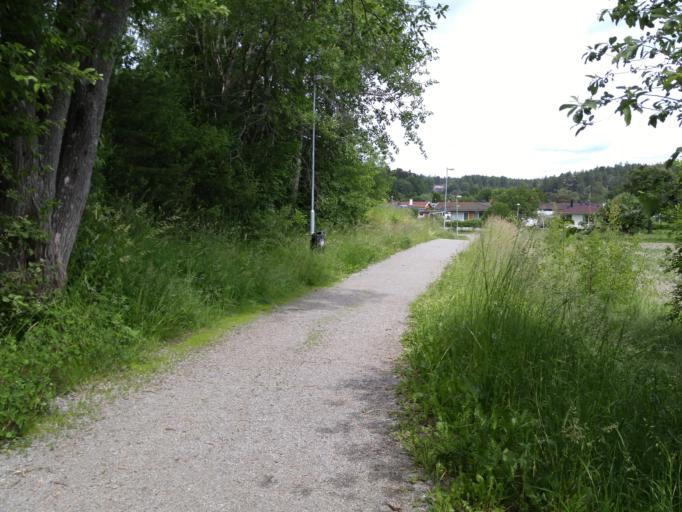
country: SE
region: Stockholm
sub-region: Sigtuna Kommun
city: Sigtuna
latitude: 59.6190
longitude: 17.7051
